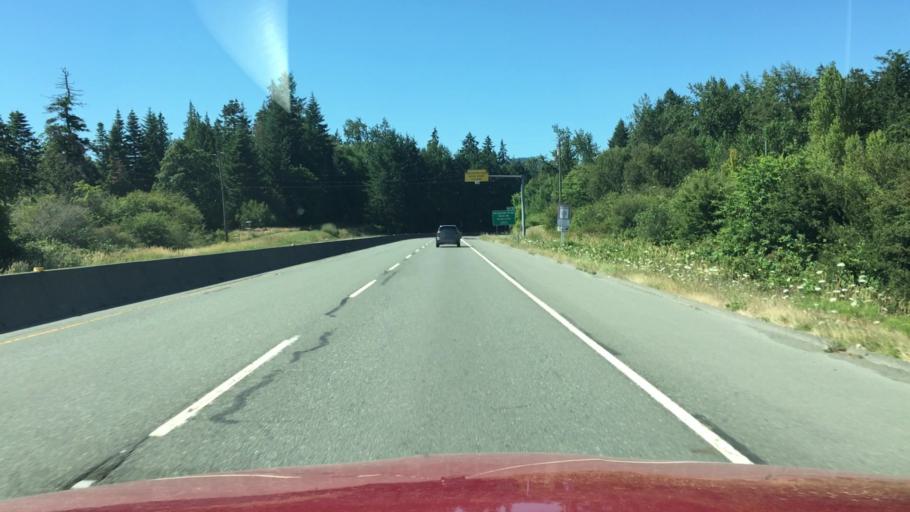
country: CA
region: British Columbia
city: North Saanich
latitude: 48.6710
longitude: -123.4268
